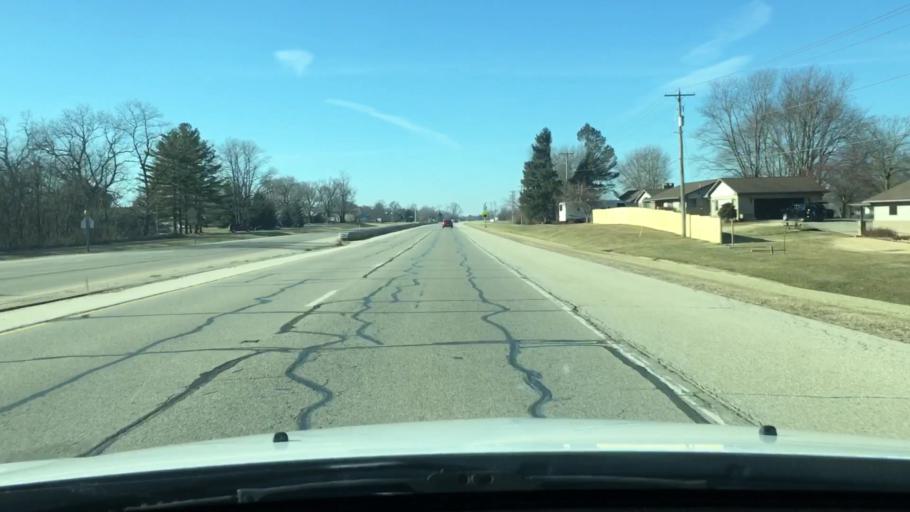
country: US
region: Illinois
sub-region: Woodford County
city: Germantown Hills
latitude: 40.7693
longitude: -89.4534
